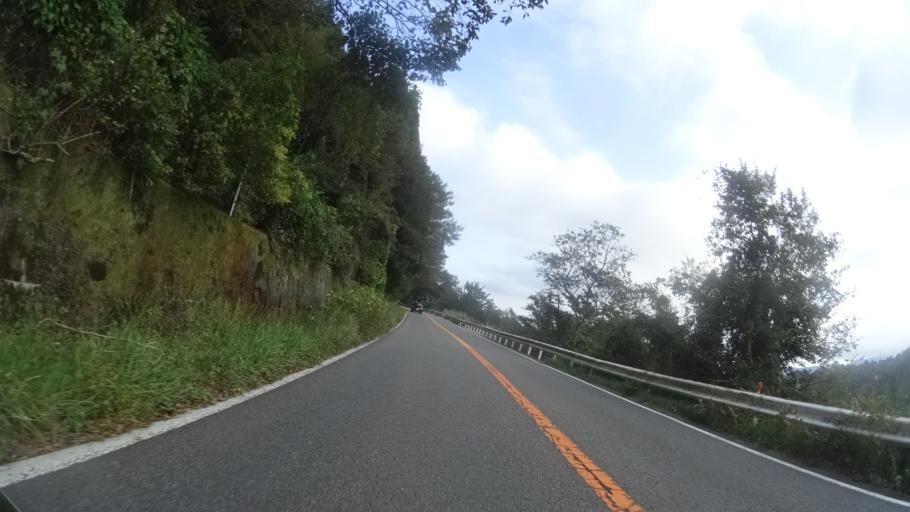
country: JP
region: Oita
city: Beppu
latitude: 33.2694
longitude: 131.4171
